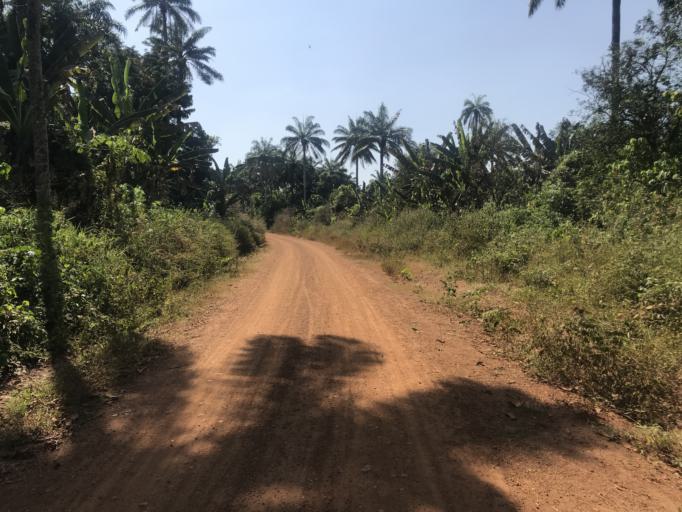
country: NG
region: Osun
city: Ikirun
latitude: 7.9339
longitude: 4.6335
